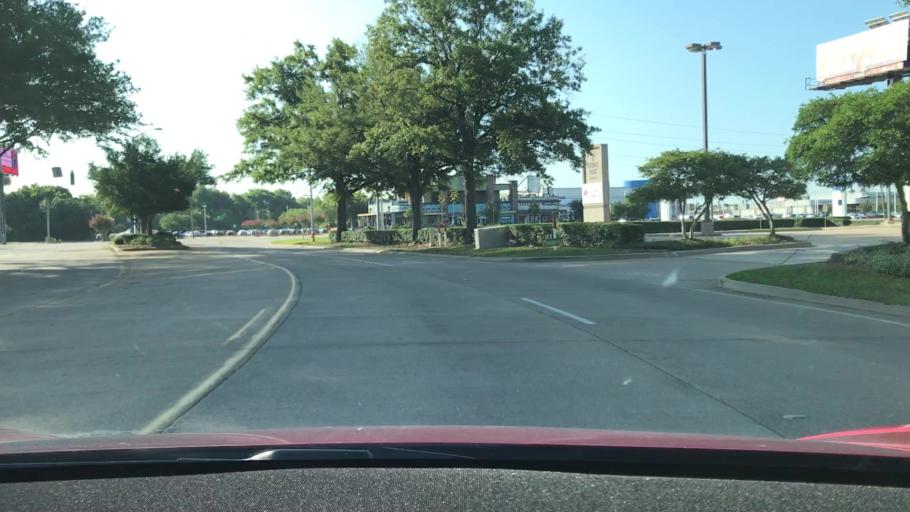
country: US
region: Louisiana
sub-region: Bossier Parish
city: Bossier City
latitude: 32.4238
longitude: -93.7211
